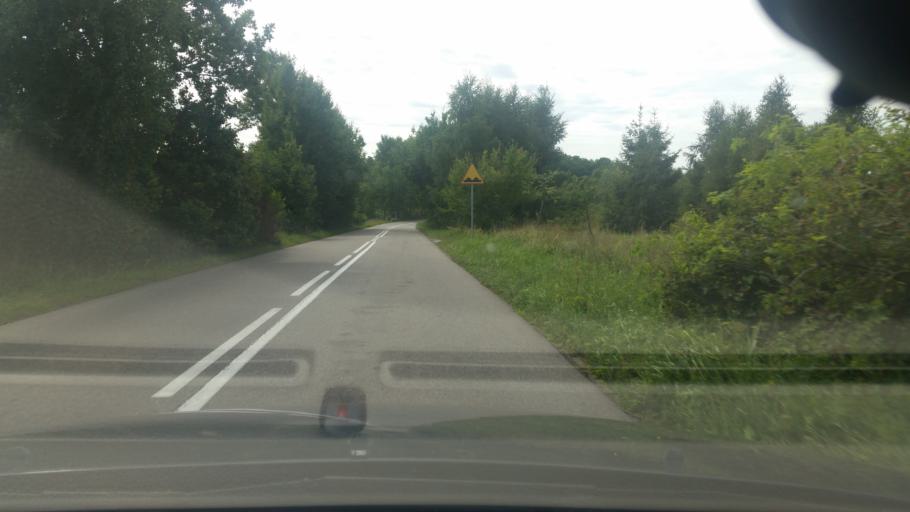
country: PL
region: Pomeranian Voivodeship
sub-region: Powiat leborski
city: Leba
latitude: 54.7477
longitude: 17.6633
